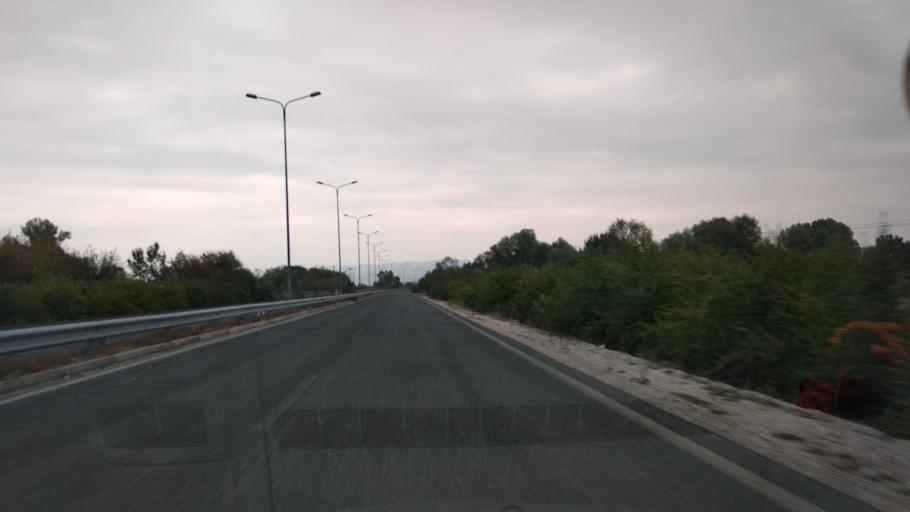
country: GR
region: Thessaly
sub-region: Trikala
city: Pyrgetos
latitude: 39.5683
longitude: 21.7403
